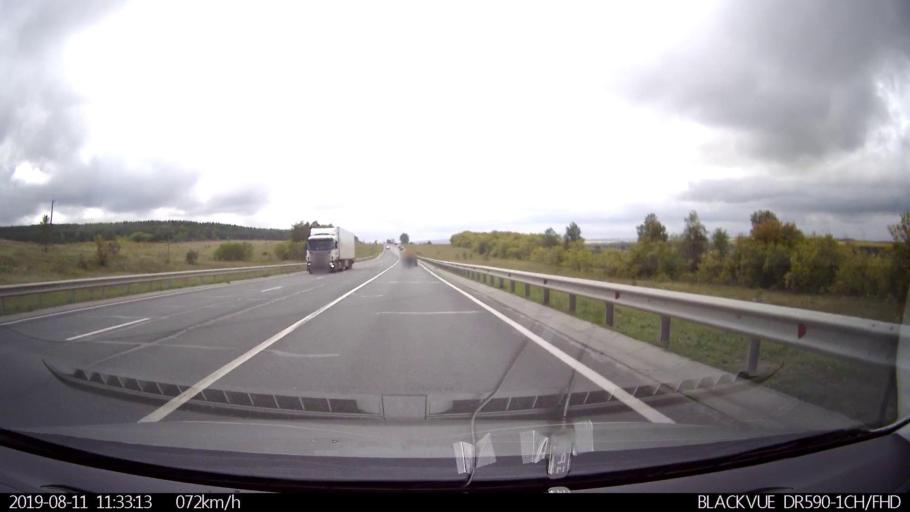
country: RU
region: Ulyanovsk
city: Krasnyy Gulyay
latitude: 54.0298
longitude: 48.2128
